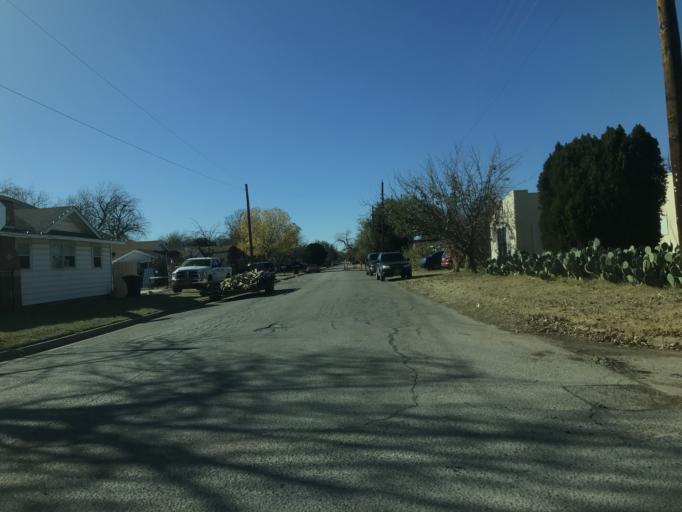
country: US
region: Texas
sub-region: Taylor County
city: Abilene
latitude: 32.4357
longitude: -99.7571
